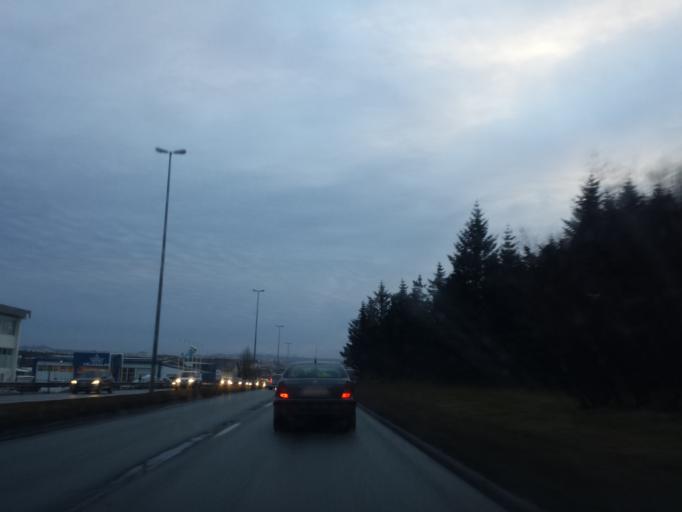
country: IS
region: Capital Region
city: Reykjavik
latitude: 64.1322
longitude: -21.8500
